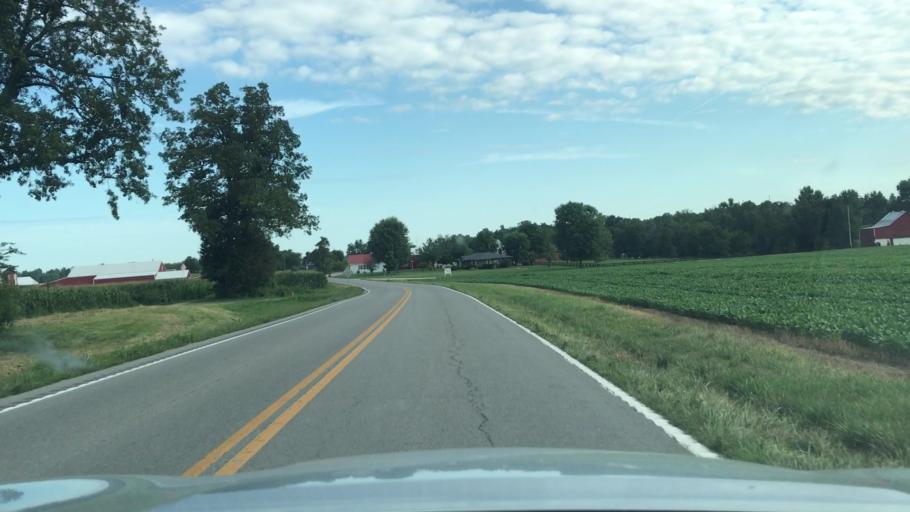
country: US
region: Kentucky
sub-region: Todd County
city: Elkton
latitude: 36.8572
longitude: -87.1588
